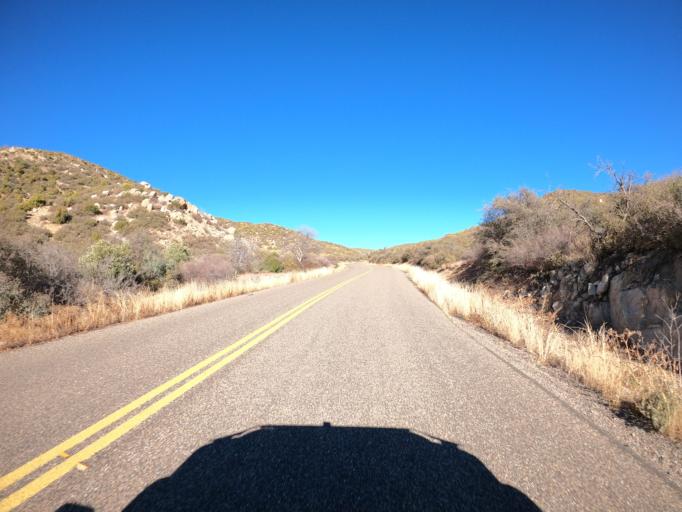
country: US
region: Arizona
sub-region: Yavapai County
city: Verde Village
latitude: 34.5649
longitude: -112.0772
